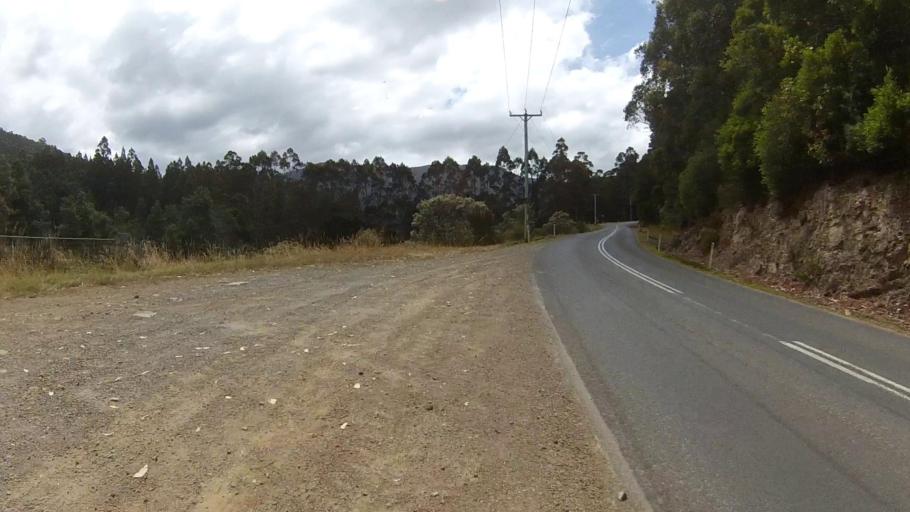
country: AU
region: Tasmania
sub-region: Huon Valley
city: Cygnet
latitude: -43.1325
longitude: 147.1562
